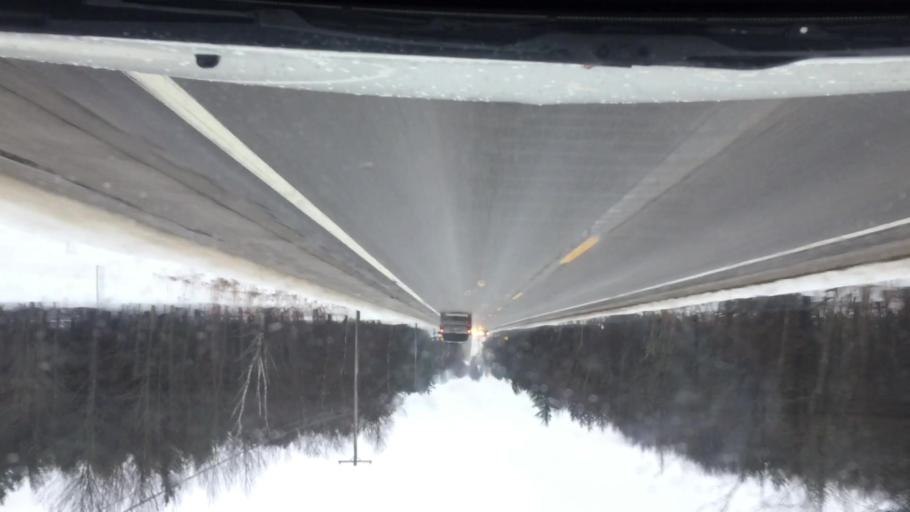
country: US
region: Michigan
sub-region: Charlevoix County
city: East Jordan
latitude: 45.2327
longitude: -85.1817
